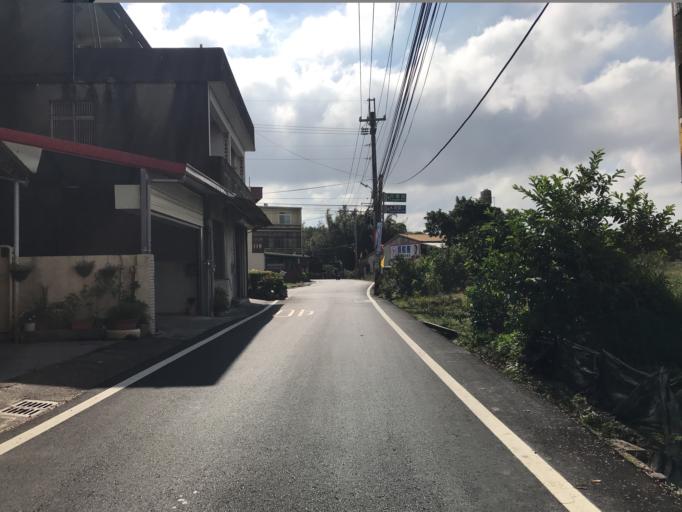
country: TW
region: Taiwan
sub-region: Hsinchu
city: Zhubei
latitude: 24.8111
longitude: 121.0023
